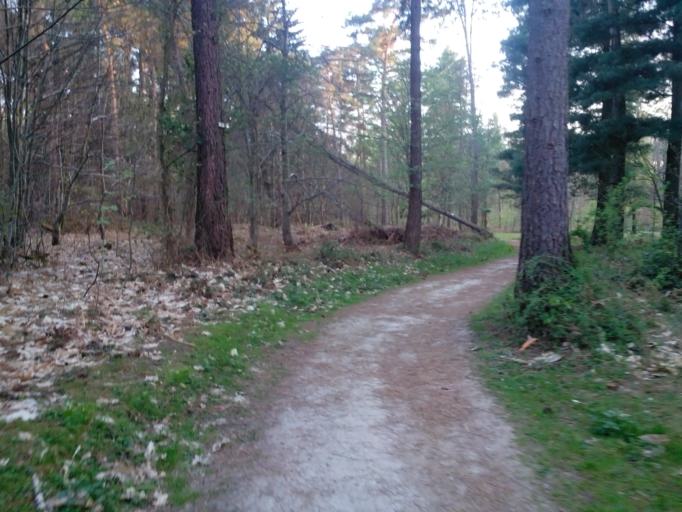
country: BE
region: Flanders
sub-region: Provincie Vlaams-Brabant
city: Oud-Heverlee
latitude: 50.8429
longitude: 4.6927
